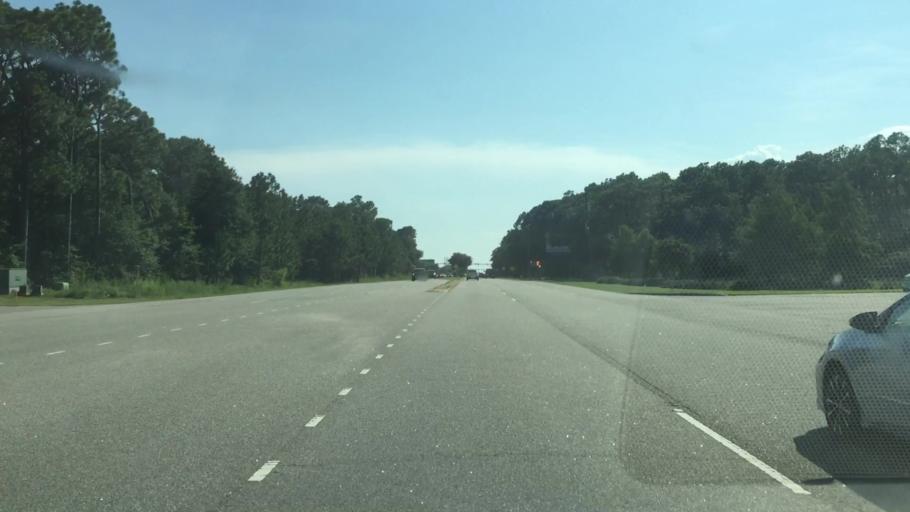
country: US
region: South Carolina
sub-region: Horry County
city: Myrtle Beach
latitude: 33.7541
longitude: -78.8103
